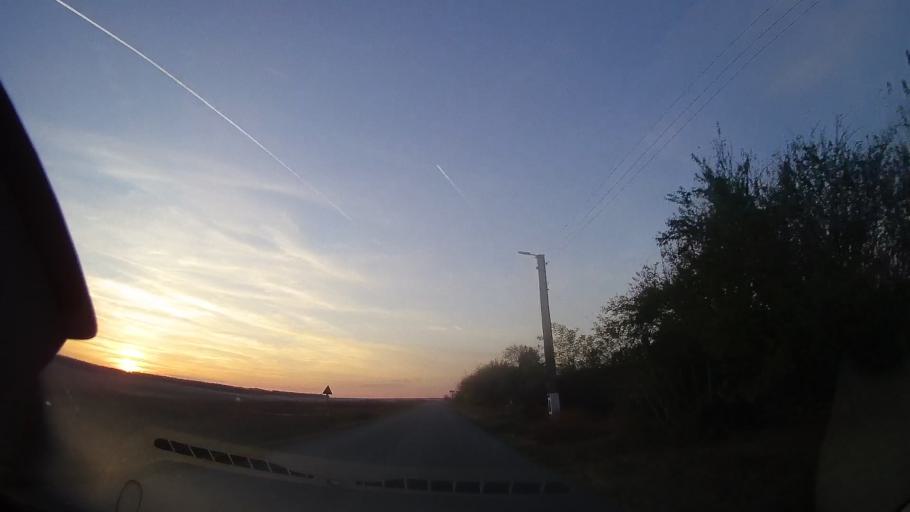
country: RO
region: Constanta
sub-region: Comuna Mereni
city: Mereni
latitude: 44.0155
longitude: 28.3127
